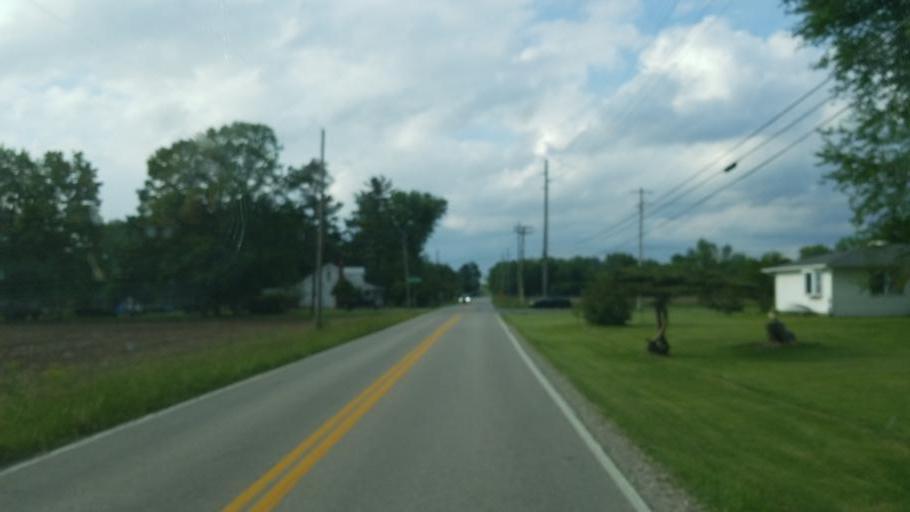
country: US
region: Ohio
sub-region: Delaware County
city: Sunbury
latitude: 40.2621
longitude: -82.7878
